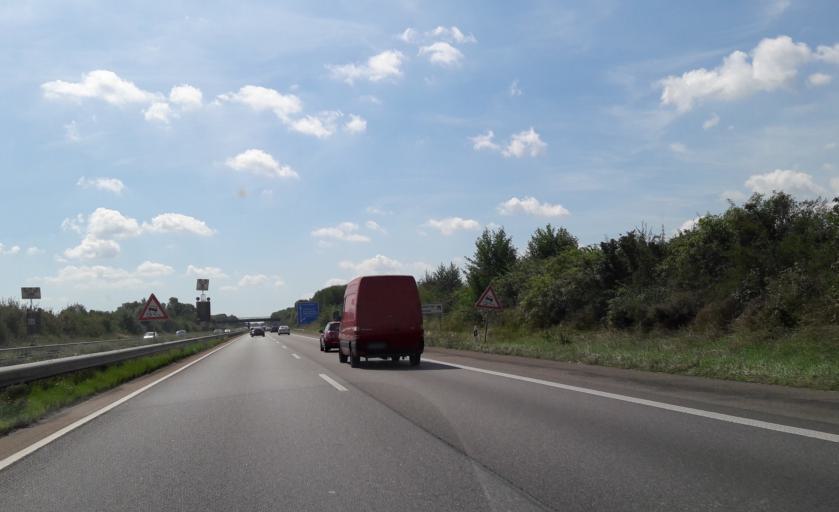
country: DE
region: Rheinland-Pfalz
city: Schifferstadt
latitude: 49.4009
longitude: 8.3408
